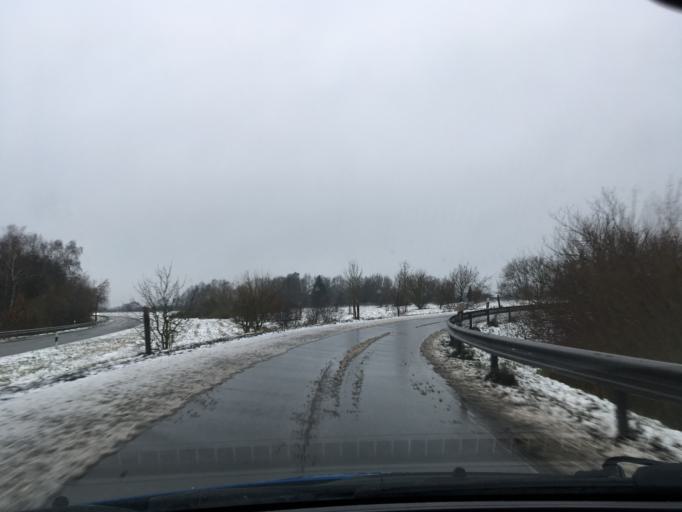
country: DE
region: Lower Saxony
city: Uelzen
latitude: 52.9839
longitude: 10.5630
